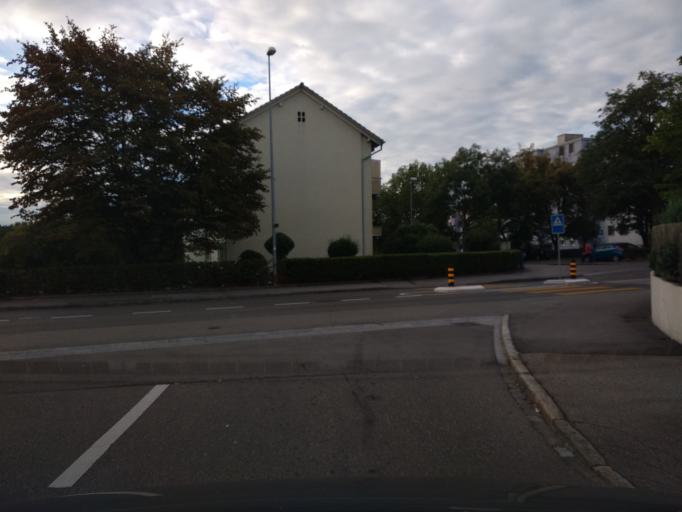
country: CH
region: Schaffhausen
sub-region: Bezirk Schaffhausen
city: Schaffhausen
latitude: 47.7171
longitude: 8.6485
